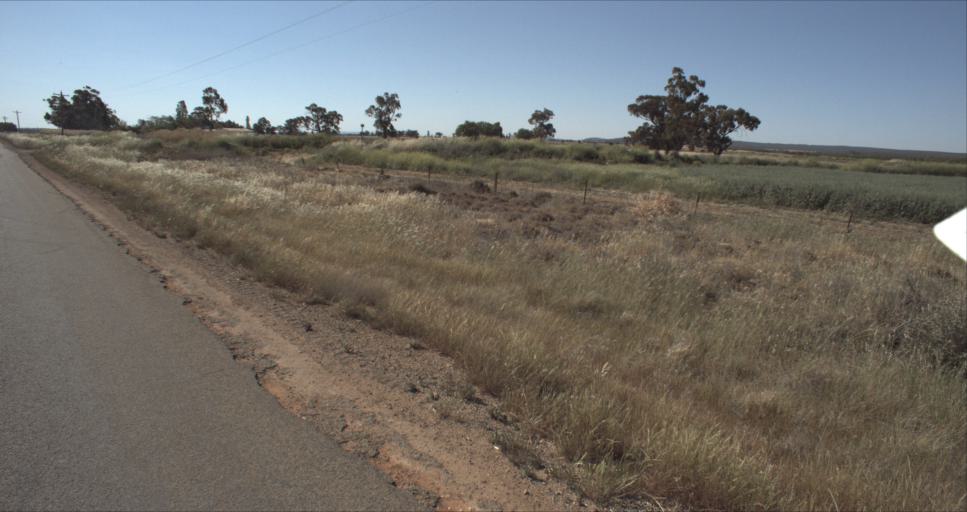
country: AU
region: New South Wales
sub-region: Leeton
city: Leeton
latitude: -34.4806
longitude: 146.3709
